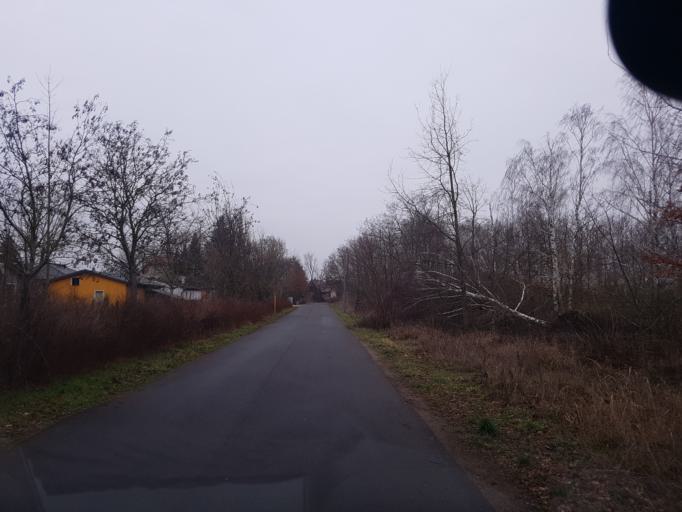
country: DE
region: Brandenburg
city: Falkenberg
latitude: 51.5916
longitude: 13.2626
